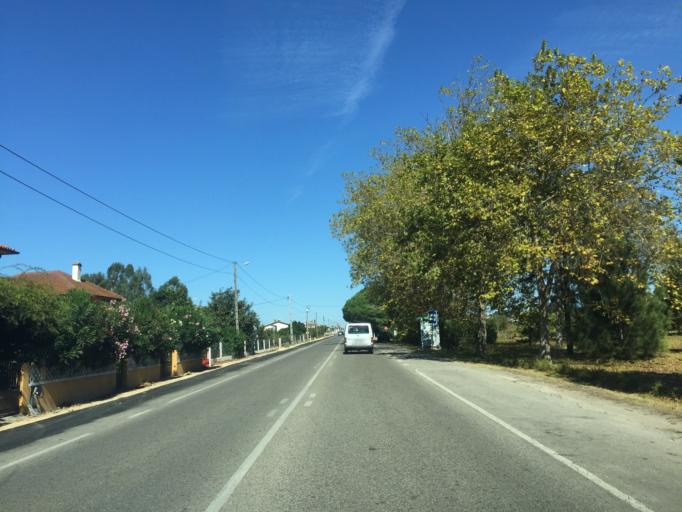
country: PT
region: Coimbra
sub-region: Montemor-O-Velho
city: Arazede
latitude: 40.2986
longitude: -8.7615
